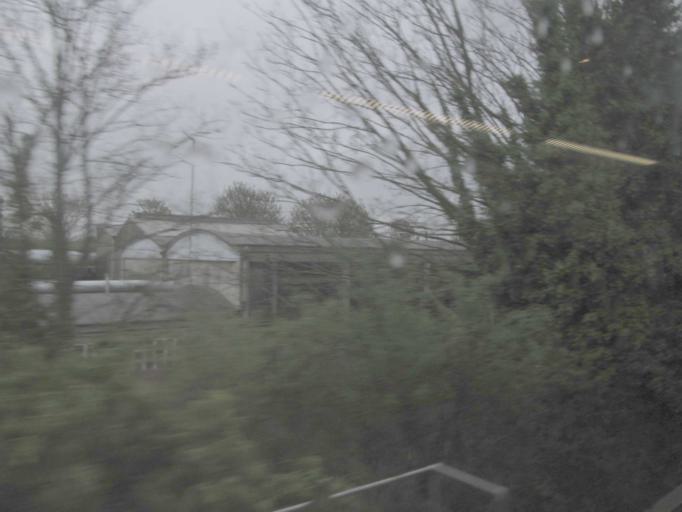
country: GB
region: England
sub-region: Reading
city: Reading
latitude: 51.4576
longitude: -0.9481
